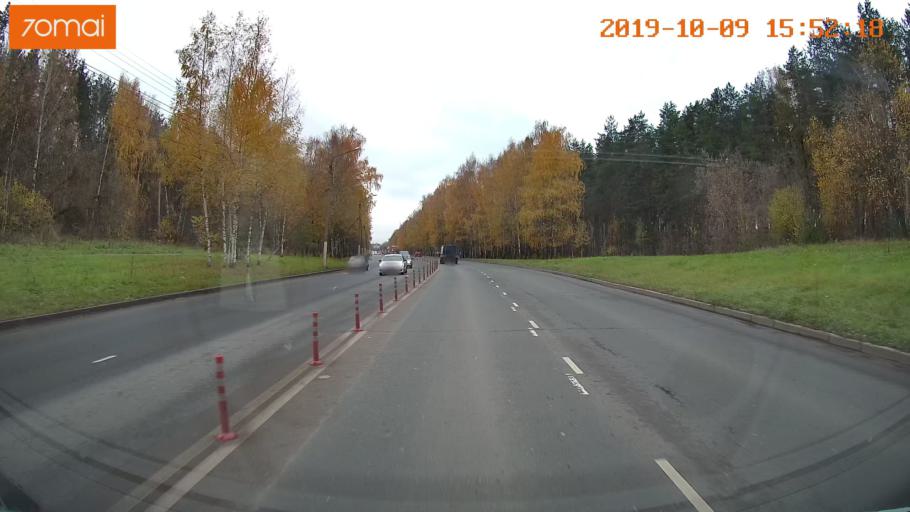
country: RU
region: Kostroma
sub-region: Kostromskoy Rayon
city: Kostroma
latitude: 57.7907
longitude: 40.9696
